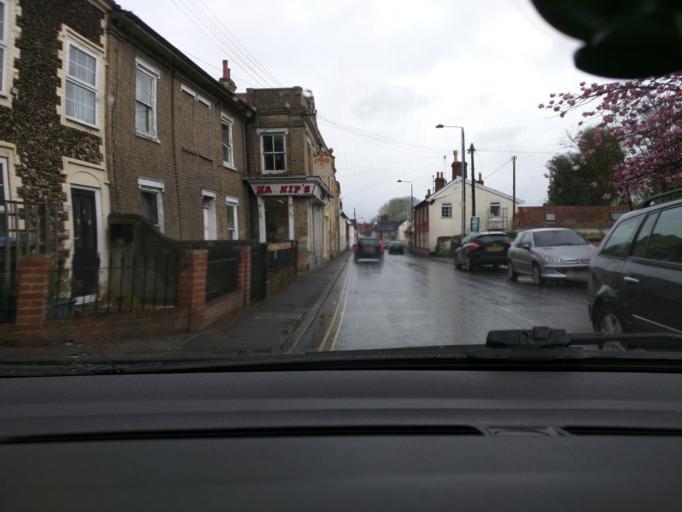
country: GB
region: England
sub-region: Suffolk
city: Wickham Market
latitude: 52.1573
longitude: 1.3670
